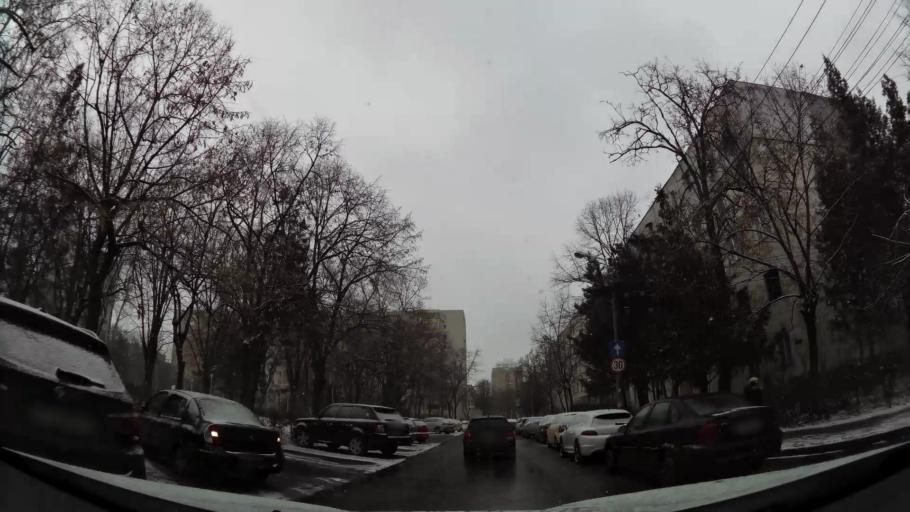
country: RO
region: Prahova
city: Ploiesti
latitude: 44.9354
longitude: 25.9867
